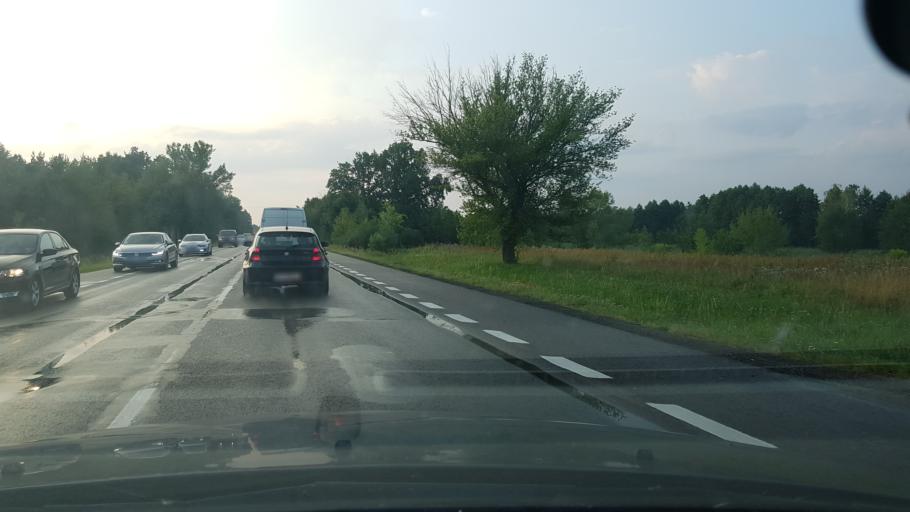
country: PL
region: Masovian Voivodeship
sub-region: Powiat ciechanowski
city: Glinojeck
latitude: 52.8127
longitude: 20.2677
